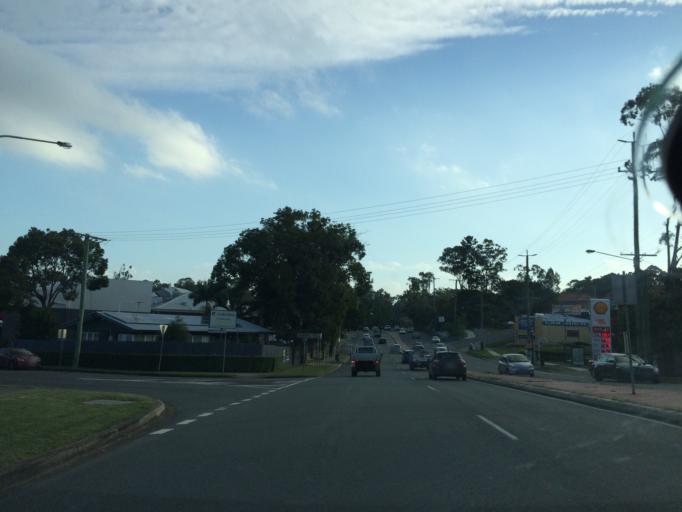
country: AU
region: Queensland
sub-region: Brisbane
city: Taringa
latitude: -27.5047
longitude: 152.9615
